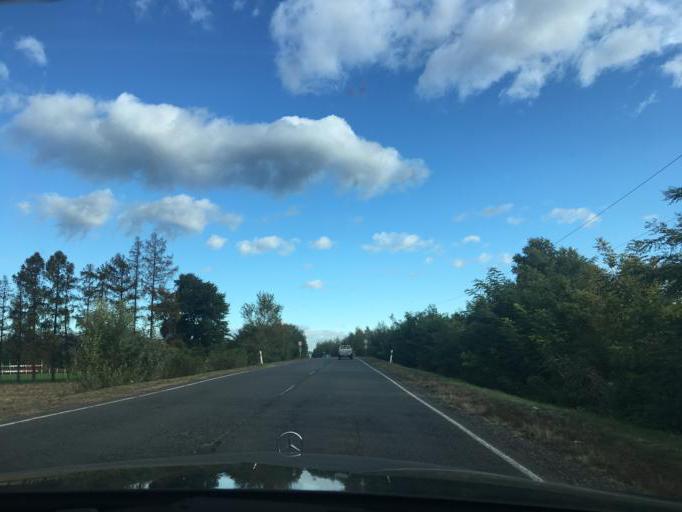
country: HU
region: Borsod-Abauj-Zemplen
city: Encs
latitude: 48.4155
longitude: 21.1779
